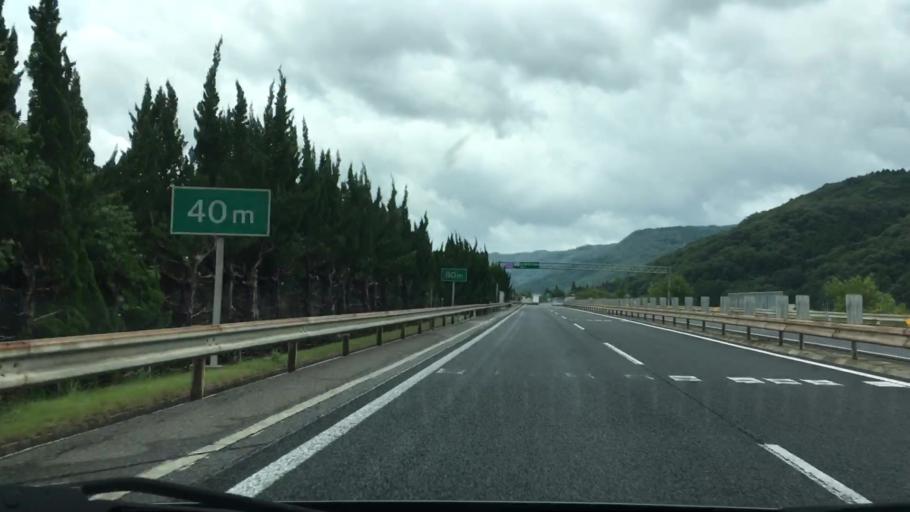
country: JP
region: Okayama
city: Niimi
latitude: 34.9722
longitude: 133.6521
